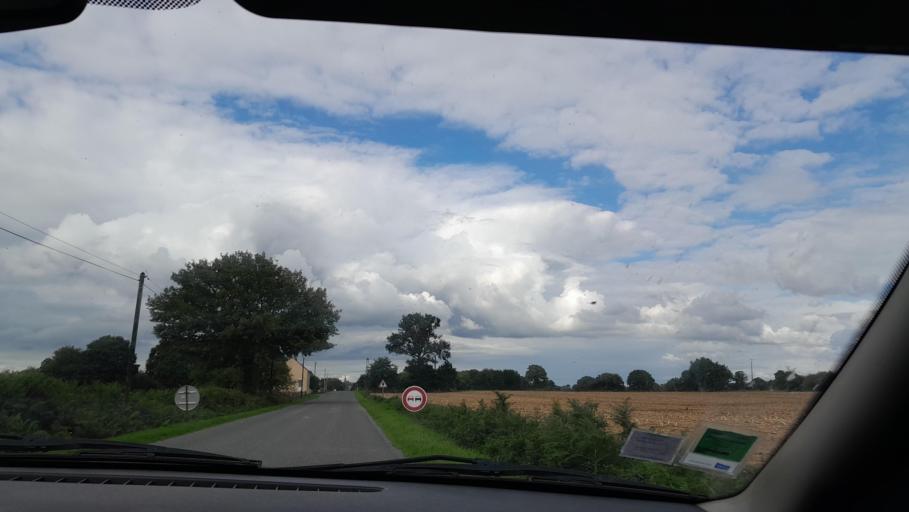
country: FR
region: Brittany
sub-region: Departement d'Ille-et-Vilaine
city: Le Pertre
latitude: 47.9854
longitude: -1.0412
